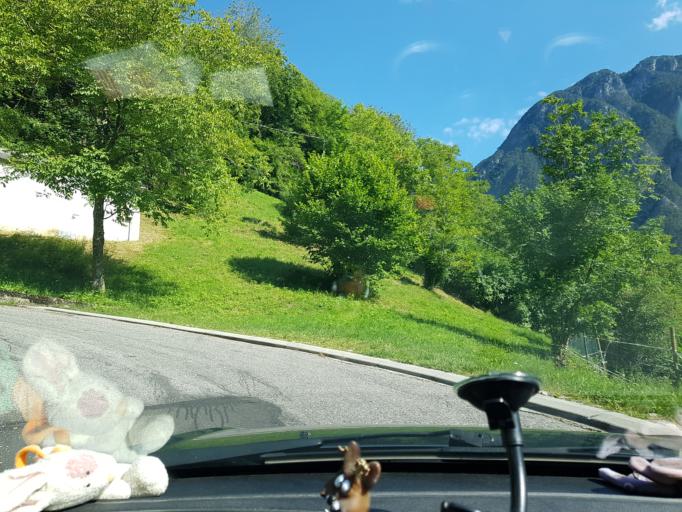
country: IT
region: Friuli Venezia Giulia
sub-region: Provincia di Udine
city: Dogna
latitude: 46.4473
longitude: 13.3126
